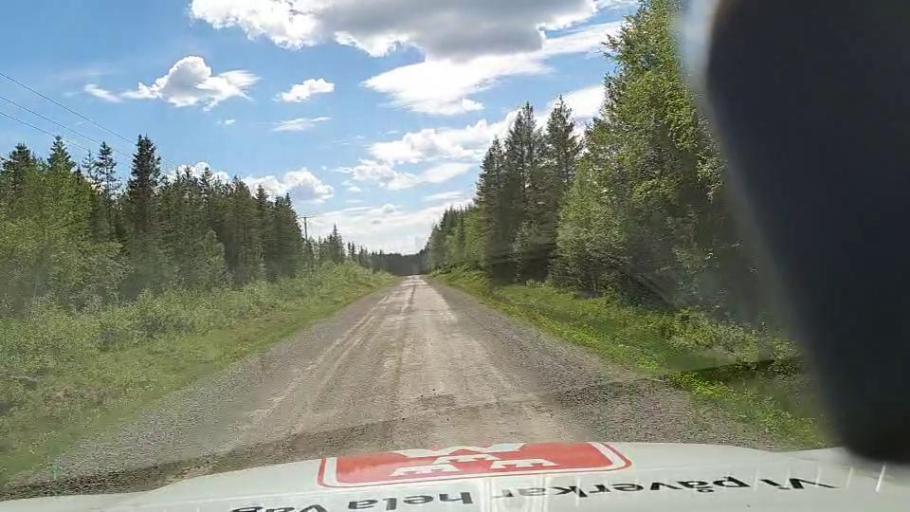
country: SE
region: Jaemtland
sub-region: Stroemsunds Kommun
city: Stroemsund
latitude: 64.5398
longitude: 15.6040
